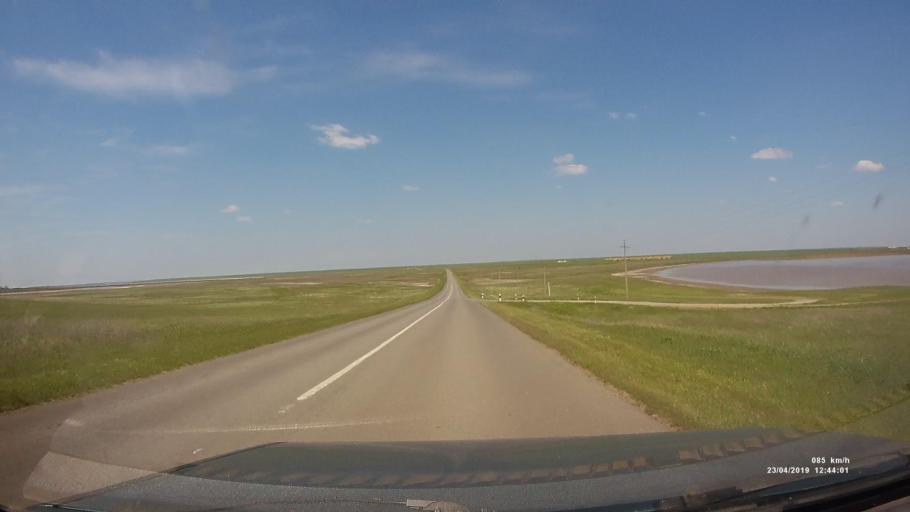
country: RU
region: Kalmykiya
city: Yashalta
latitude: 46.4715
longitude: 42.6497
